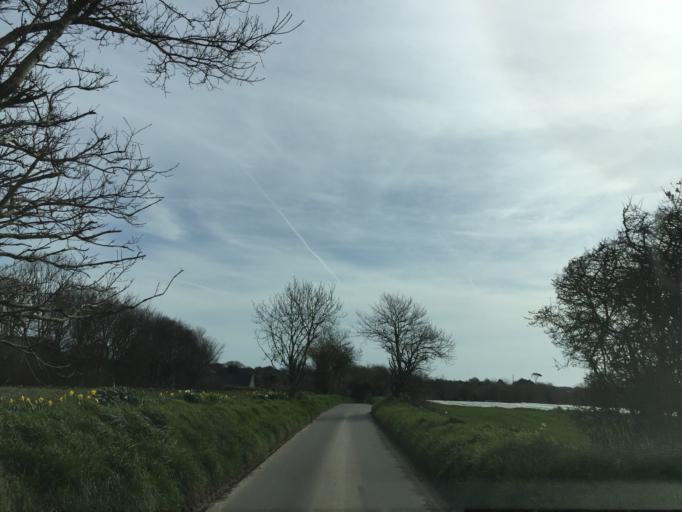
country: JE
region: St Helier
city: Saint Helier
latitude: 49.2279
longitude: -2.1263
